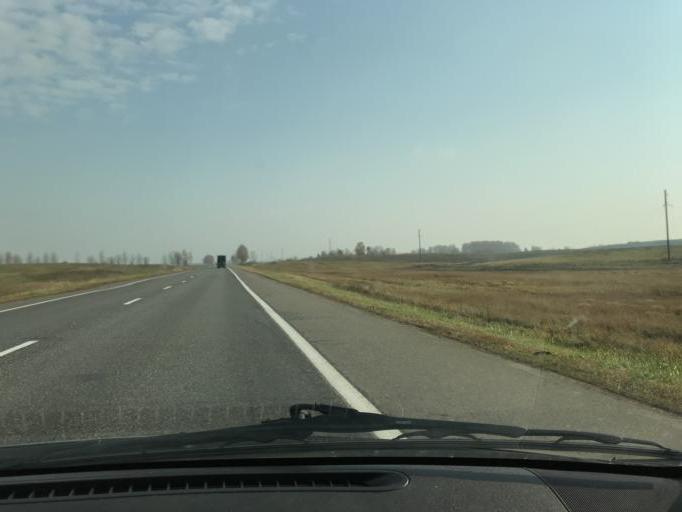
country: BY
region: Vitebsk
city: Chashniki
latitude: 55.0133
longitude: 29.0933
